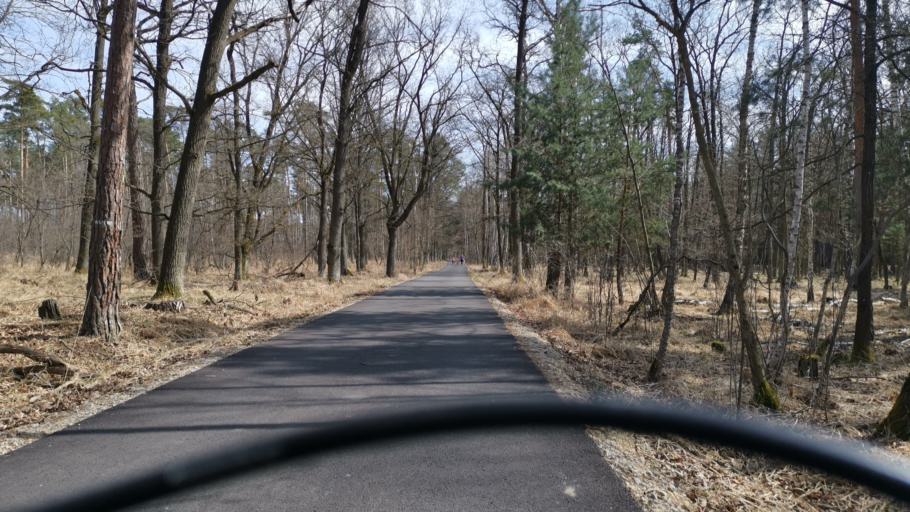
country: SK
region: Trnavsky
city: Gbely
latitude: 48.7115
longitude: 17.0630
